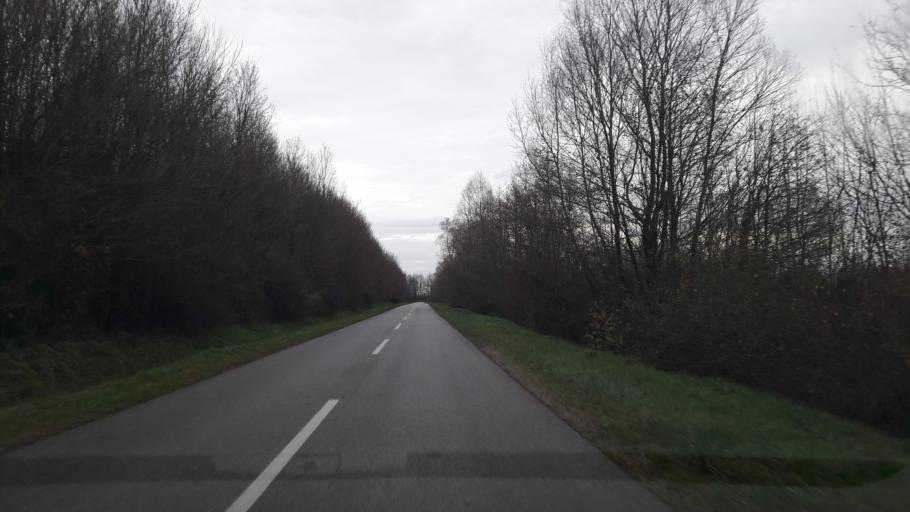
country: HR
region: Osjecko-Baranjska
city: Velimirovac
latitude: 45.6319
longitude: 18.1050
